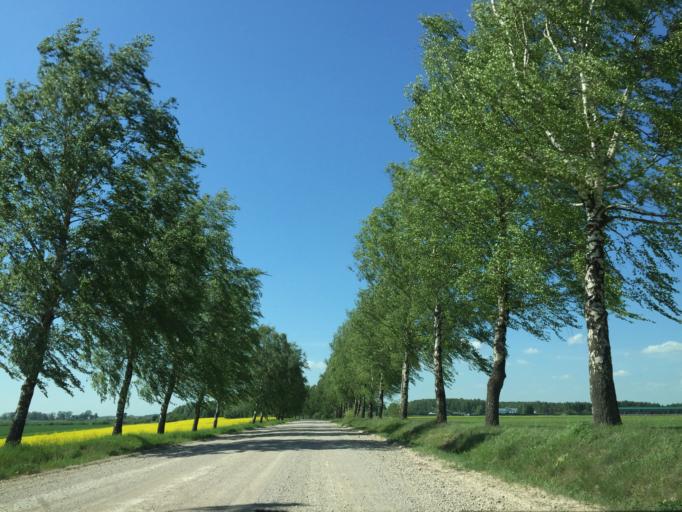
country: LV
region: Rundales
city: Pilsrundale
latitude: 56.5320
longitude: 24.0078
